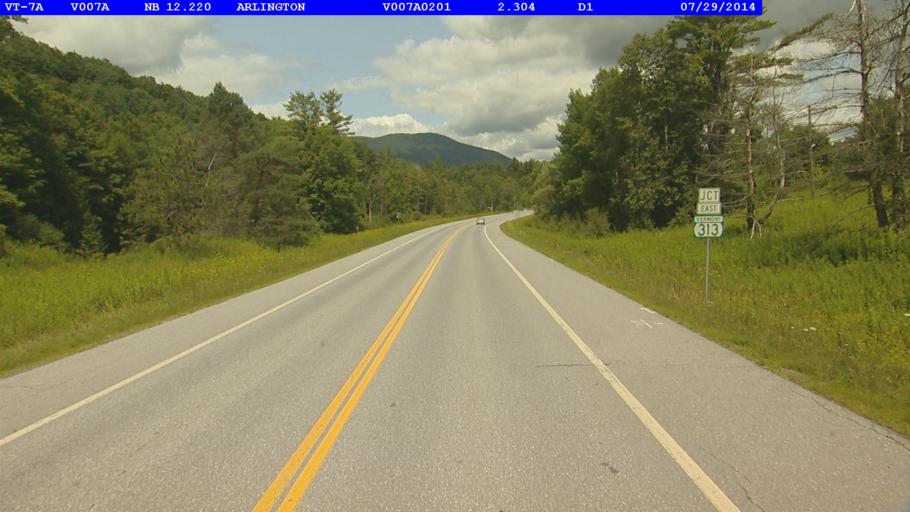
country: US
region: Vermont
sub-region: Bennington County
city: Arlington
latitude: 43.0532
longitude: -73.1633
